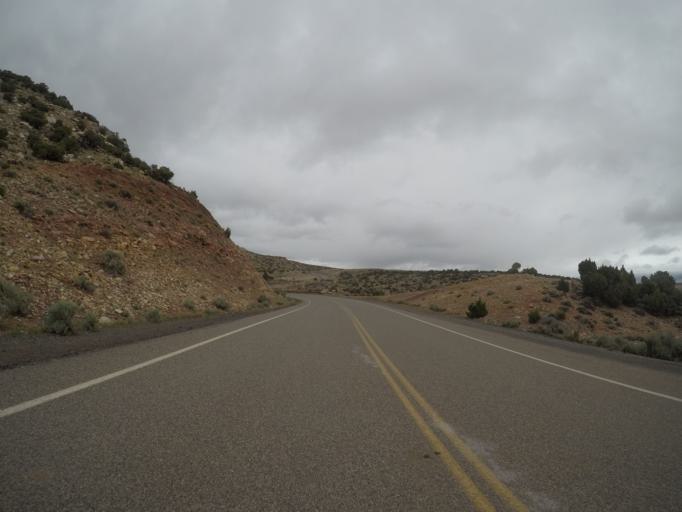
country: US
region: Wyoming
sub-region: Big Horn County
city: Lovell
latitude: 45.0442
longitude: -108.2526
